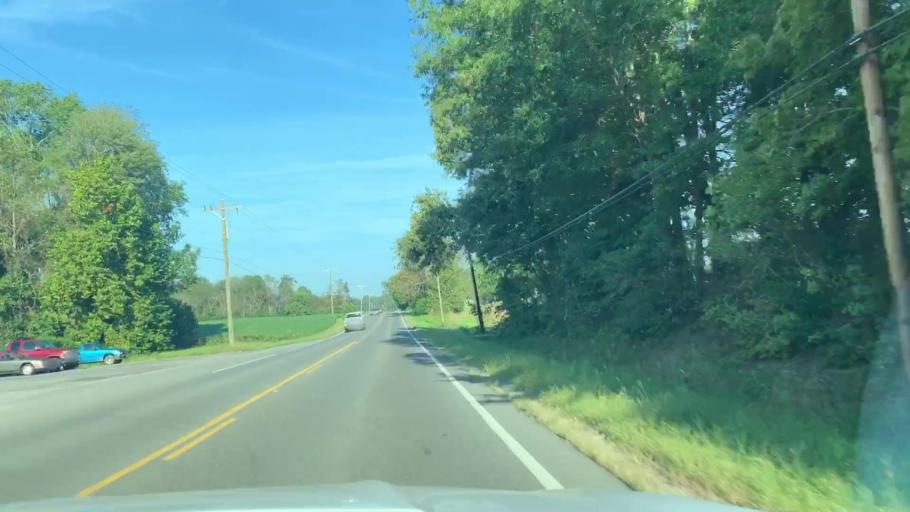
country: US
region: Virginia
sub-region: Lancaster County
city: Lancaster
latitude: 37.7654
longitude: -76.4280
